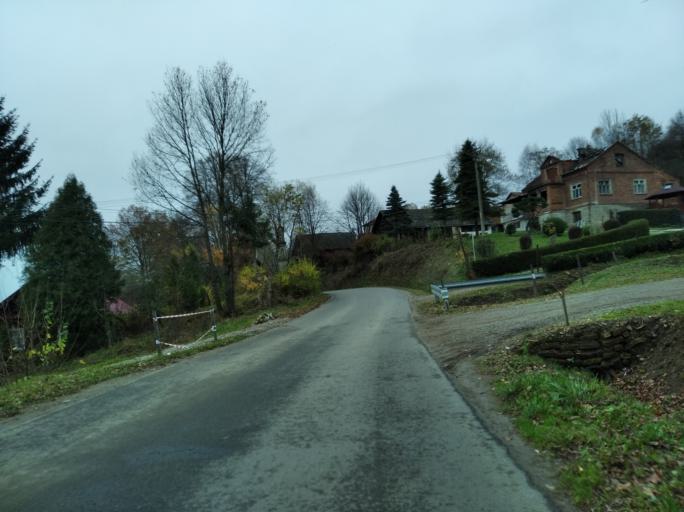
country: PL
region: Subcarpathian Voivodeship
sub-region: Powiat strzyzowski
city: Frysztak
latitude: 49.8291
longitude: 21.6345
